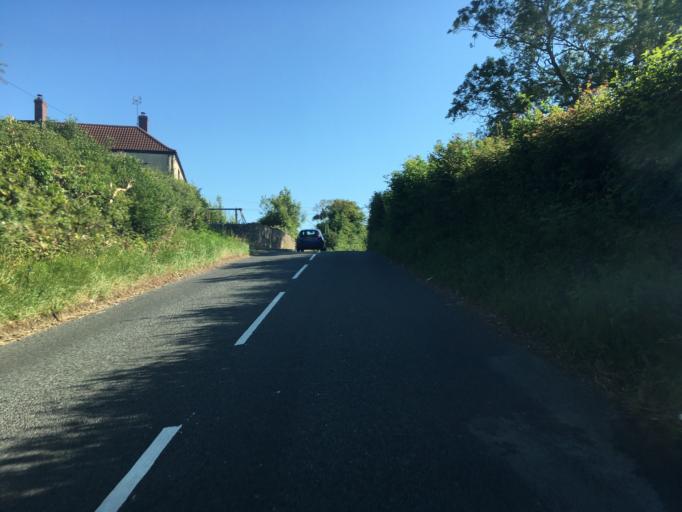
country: GB
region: England
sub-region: South Gloucestershire
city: Pucklechurch
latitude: 51.4622
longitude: -2.4273
